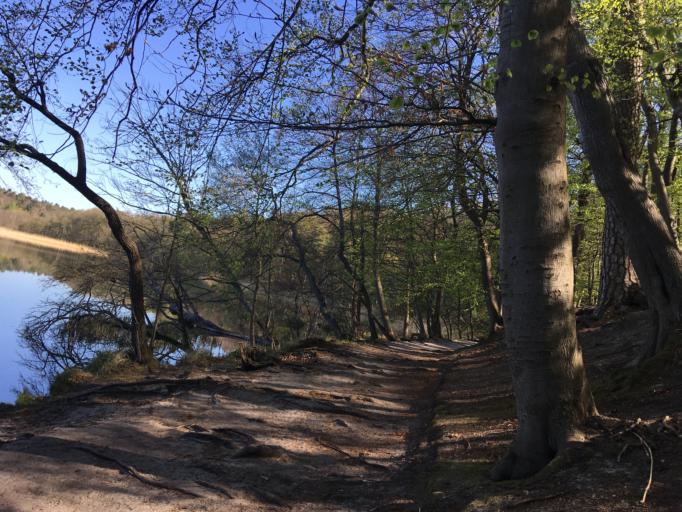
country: DE
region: Brandenburg
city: Wandlitz
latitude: 52.7498
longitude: 13.5290
